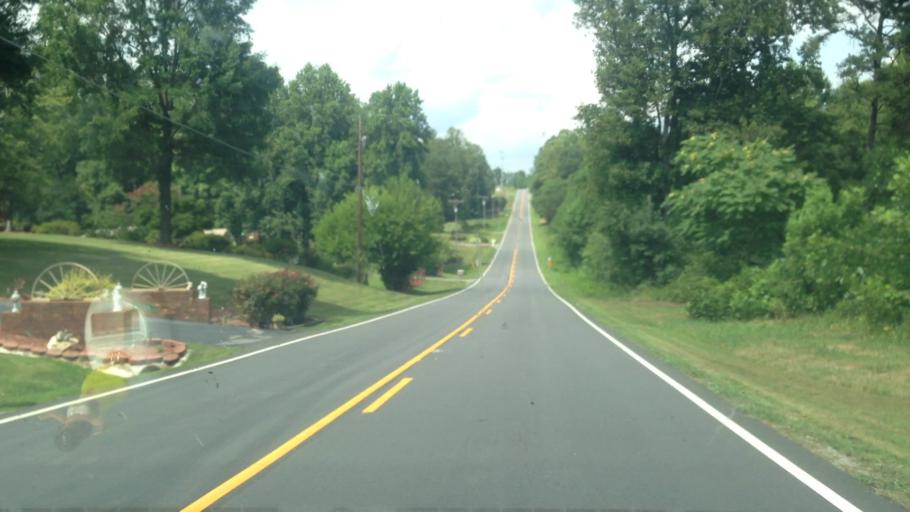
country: US
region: North Carolina
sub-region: Rockingham County
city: Mayodan
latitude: 36.4154
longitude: -80.0864
